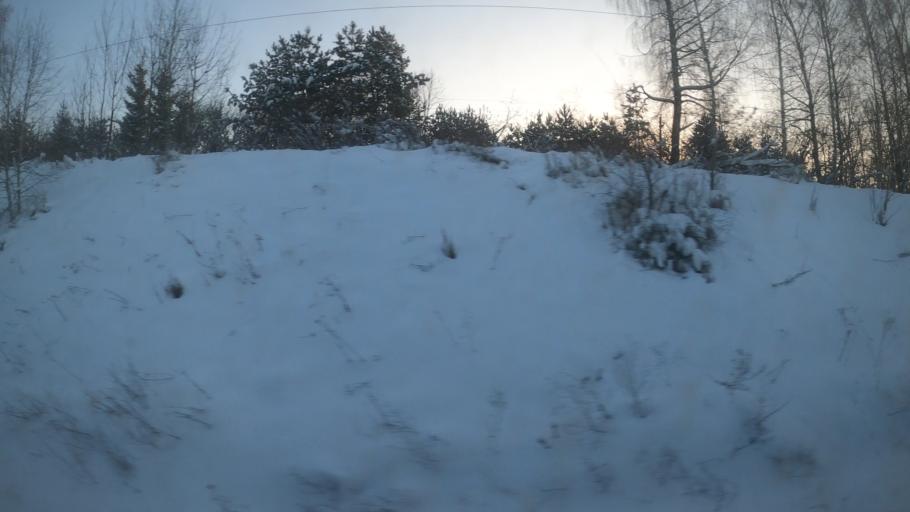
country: RU
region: Moskovskaya
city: Dedenevo
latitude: 56.2558
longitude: 37.5062
